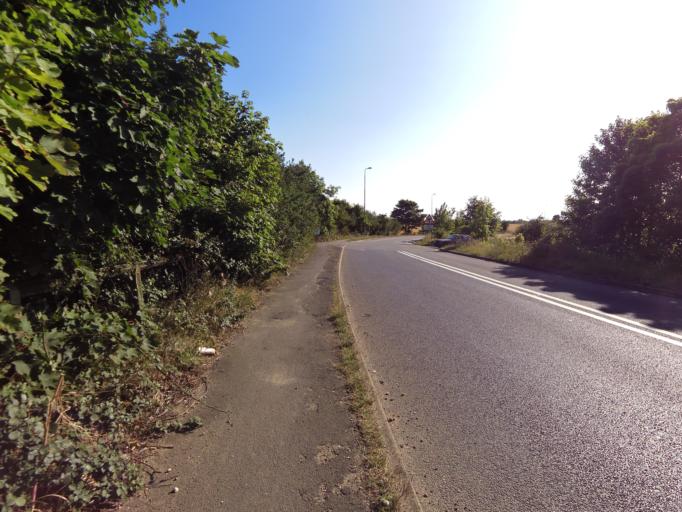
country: GB
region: England
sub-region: Essex
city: Hatfield Peverel
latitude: 51.7837
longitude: 0.6175
